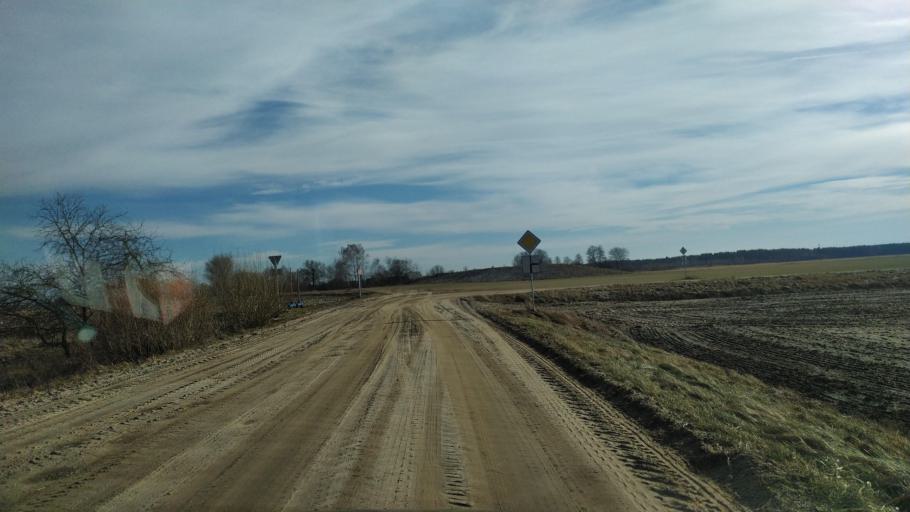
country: BY
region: Brest
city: Pruzhany
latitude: 52.5755
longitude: 24.3023
